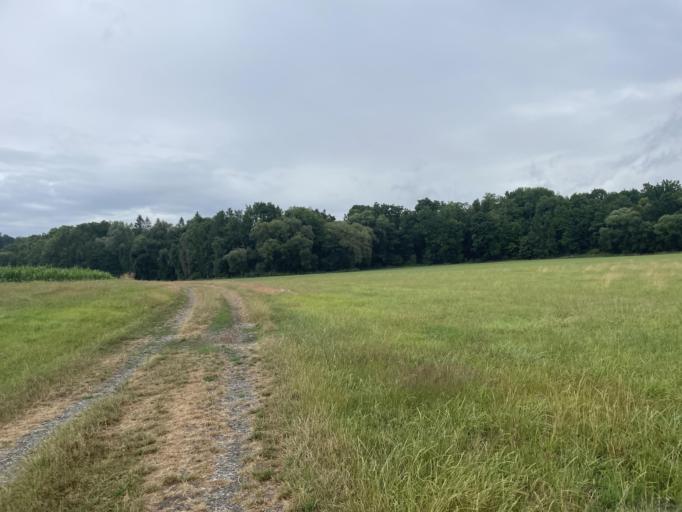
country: DE
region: Bavaria
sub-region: Upper Franconia
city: Neunkirchen am Main
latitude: 49.9385
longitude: 11.6278
